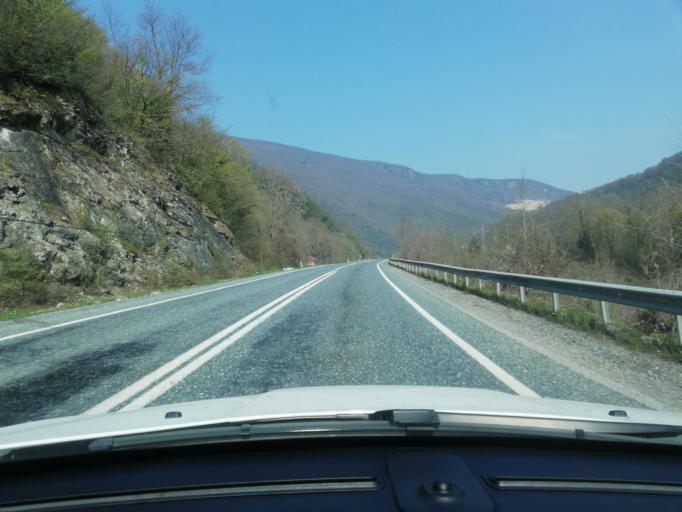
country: TR
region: Zonguldak
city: Gokcebey
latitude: 41.2581
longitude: 32.1561
